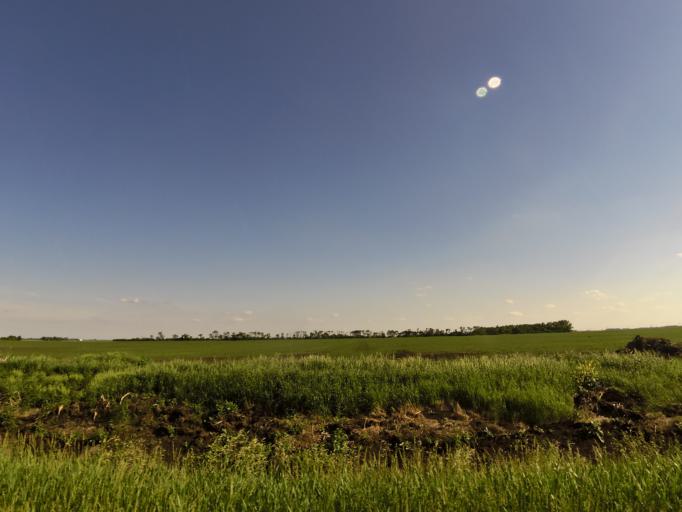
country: US
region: North Dakota
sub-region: Walsh County
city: Grafton
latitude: 48.3975
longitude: -97.2506
